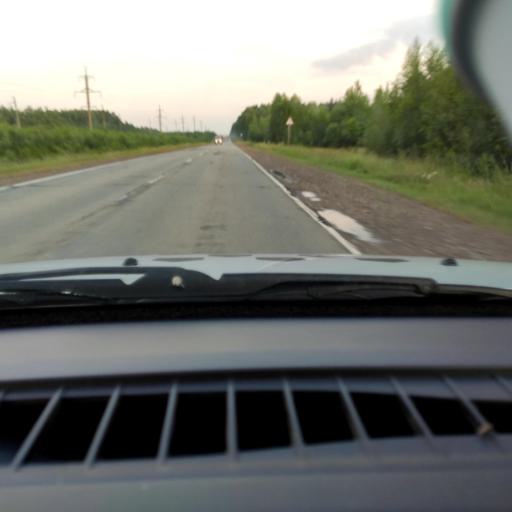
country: RU
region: Udmurtiya
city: Fakel
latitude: 57.6316
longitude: 53.0404
